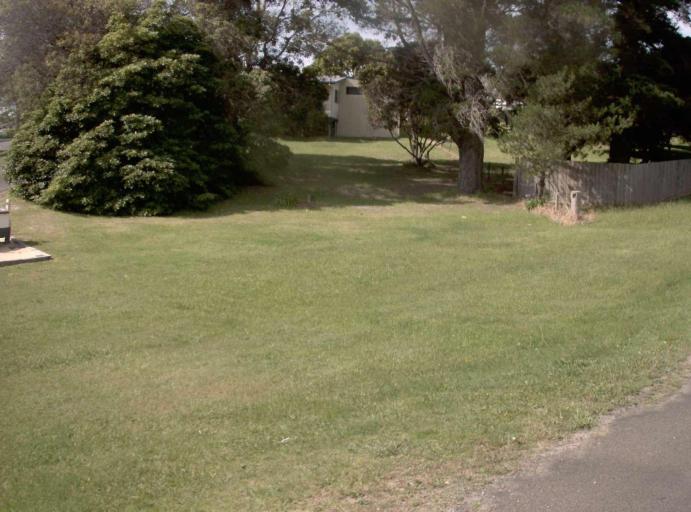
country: AU
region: Victoria
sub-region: East Gippsland
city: Lakes Entrance
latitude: -37.8657
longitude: 148.0205
